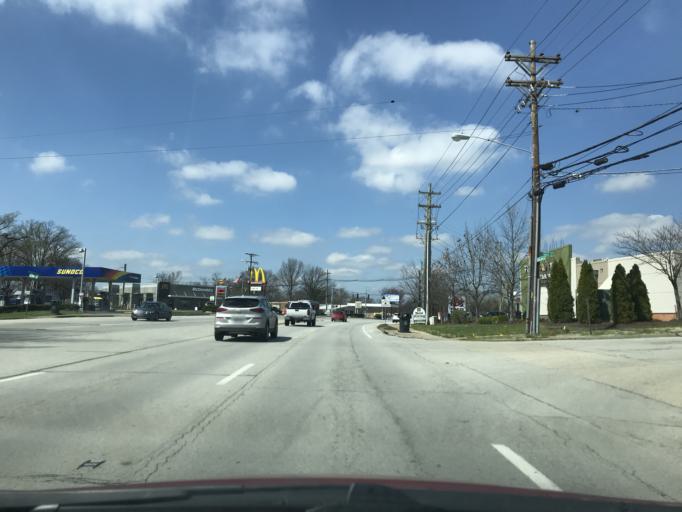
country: US
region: Kentucky
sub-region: Jefferson County
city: Audubon Park
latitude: 38.2114
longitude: -85.7191
